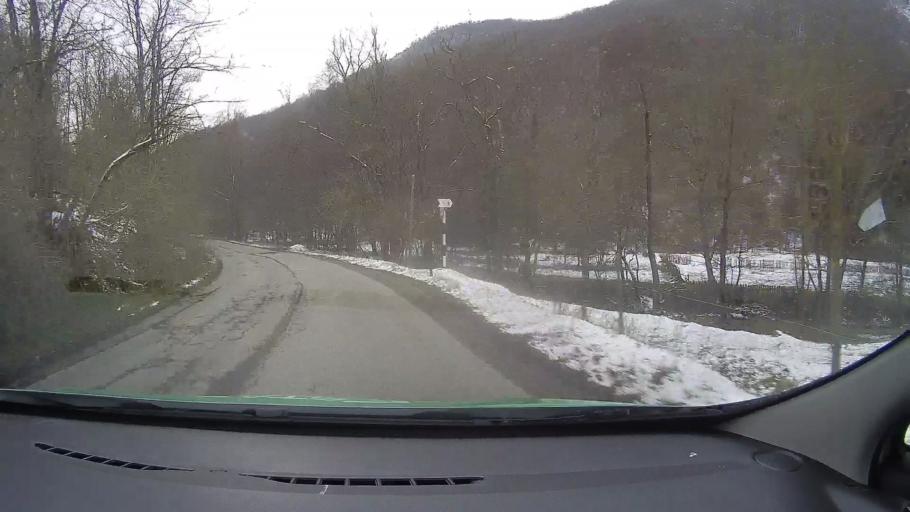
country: RO
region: Hunedoara
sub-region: Comuna Balsa
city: Balsa
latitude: 46.0138
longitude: 23.1496
